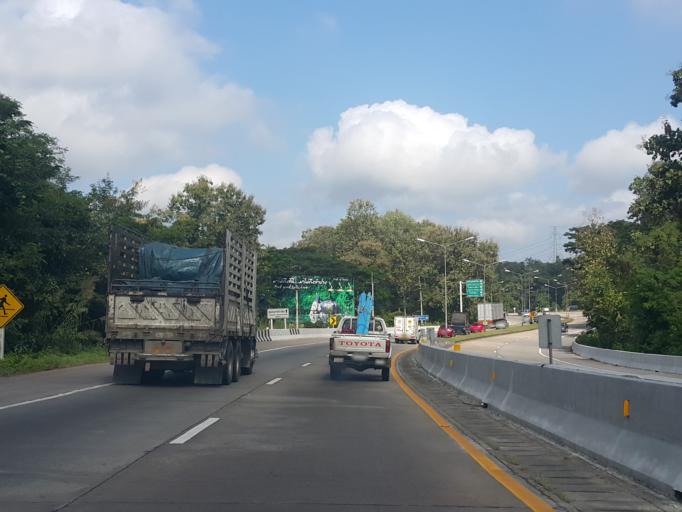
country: TH
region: Lampang
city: Hang Chat
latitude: 18.3509
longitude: 99.2434
